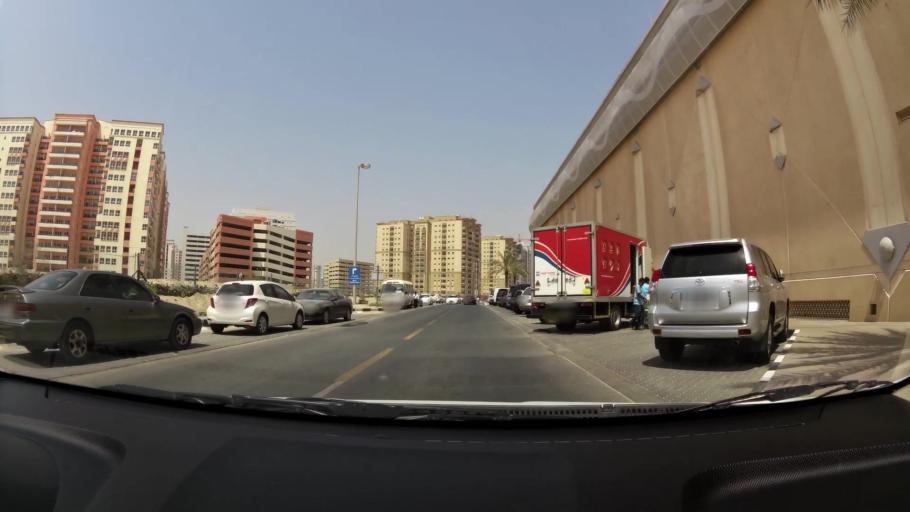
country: AE
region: Ash Shariqah
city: Sharjah
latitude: 25.2971
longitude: 55.3730
